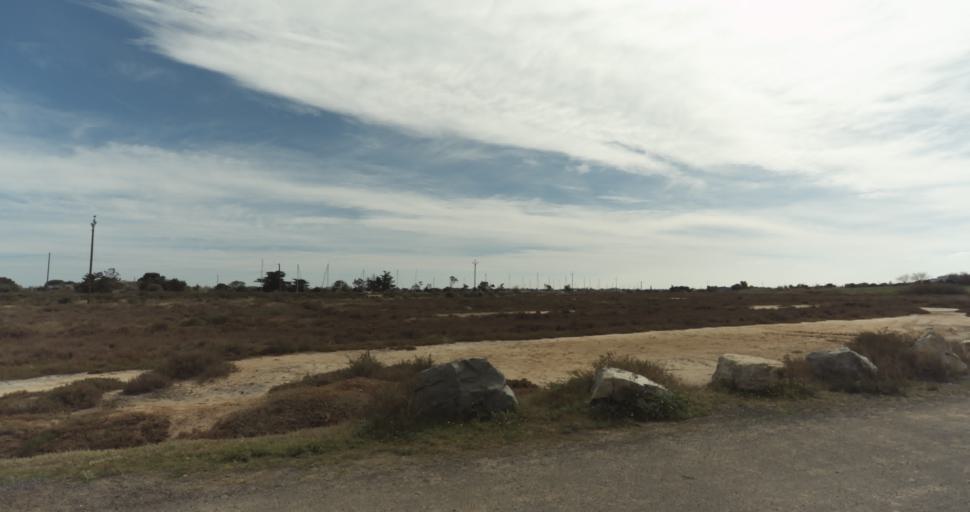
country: FR
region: Languedoc-Roussillon
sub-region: Departement de l'Herault
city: Marseillan
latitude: 43.3357
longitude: 3.5358
